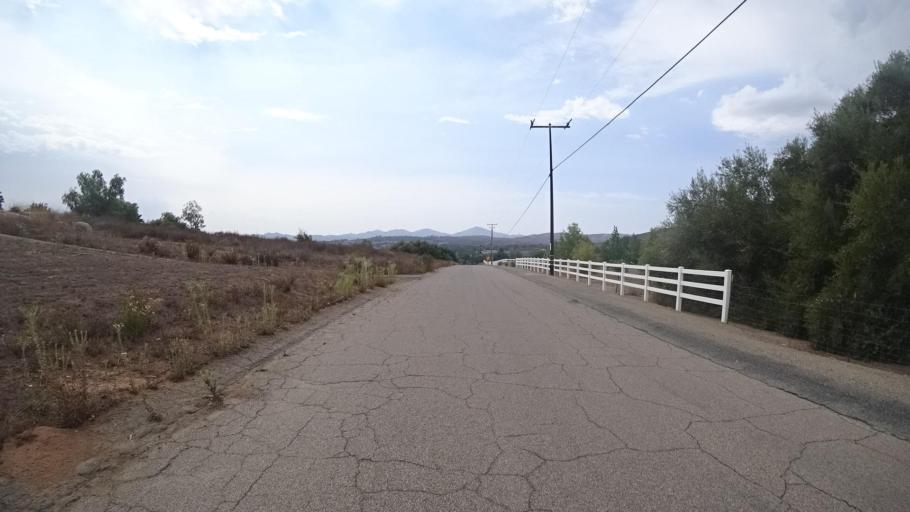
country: US
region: California
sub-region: San Diego County
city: Ramona
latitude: 33.0851
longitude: -116.8532
